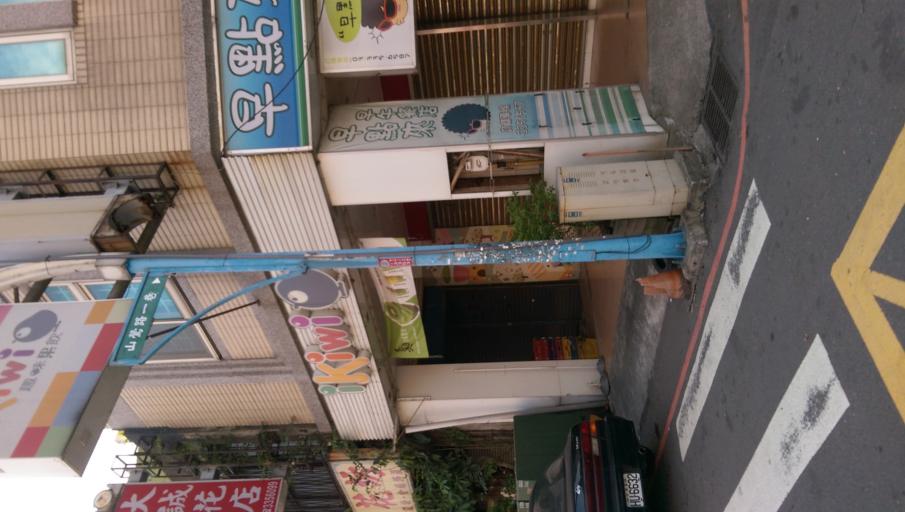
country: TW
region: Taiwan
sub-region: Taoyuan
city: Taoyuan
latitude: 24.9916
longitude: 121.3228
